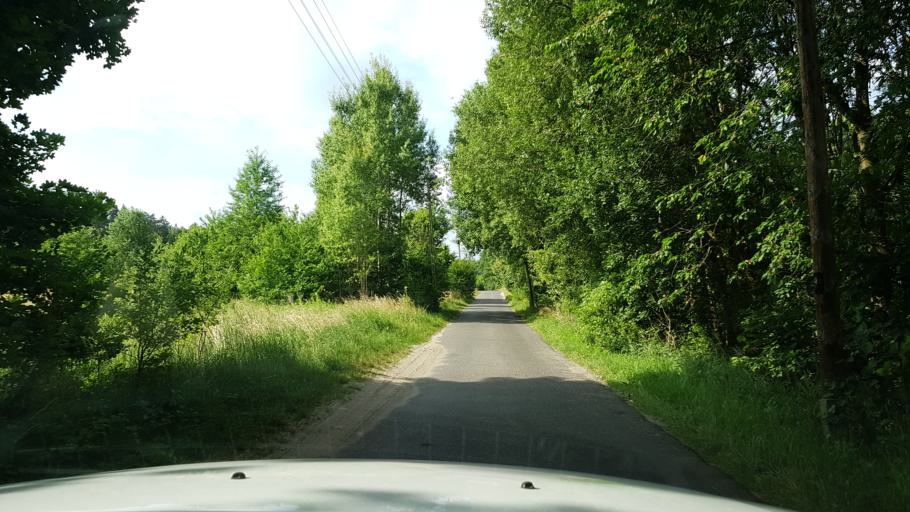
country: PL
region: West Pomeranian Voivodeship
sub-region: Powiat gryfinski
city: Gryfino
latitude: 53.2533
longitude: 14.5526
